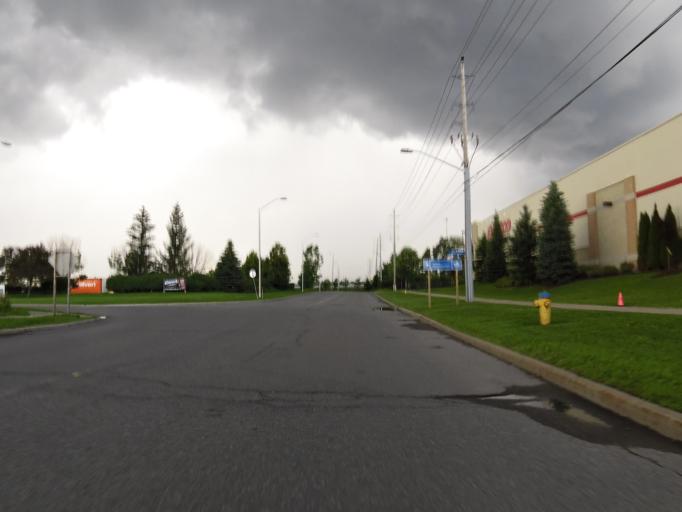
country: CA
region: Ontario
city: Bells Corners
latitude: 45.3023
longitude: -75.9137
